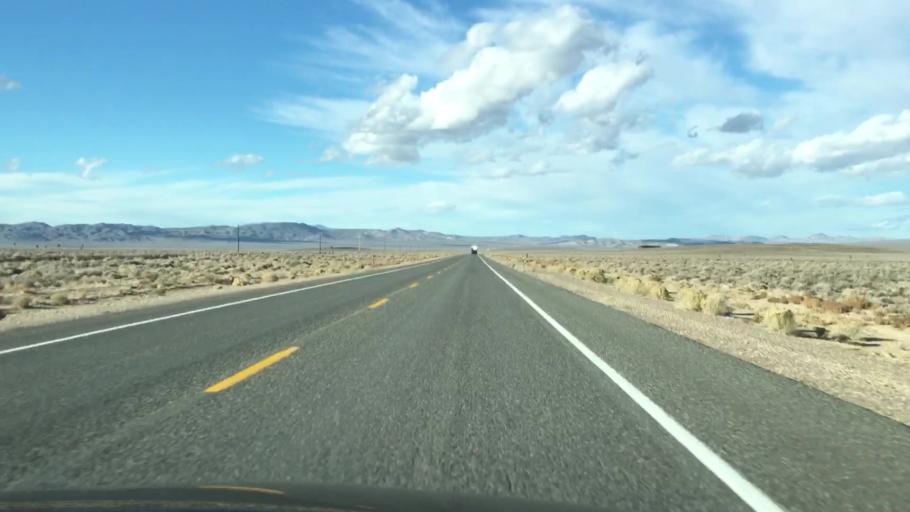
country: US
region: Nevada
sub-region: Esmeralda County
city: Goldfield
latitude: 37.4078
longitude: -117.1516
